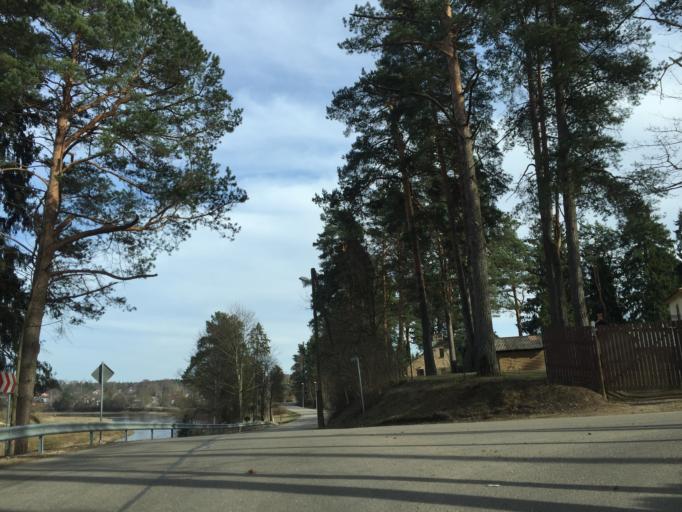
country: LV
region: Ogre
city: Ogre
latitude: 56.8110
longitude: 24.6290
